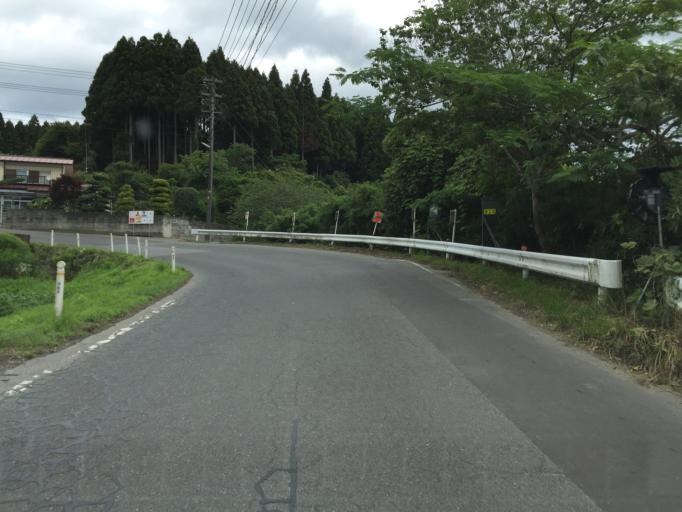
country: JP
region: Fukushima
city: Namie
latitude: 37.6557
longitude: 140.9635
